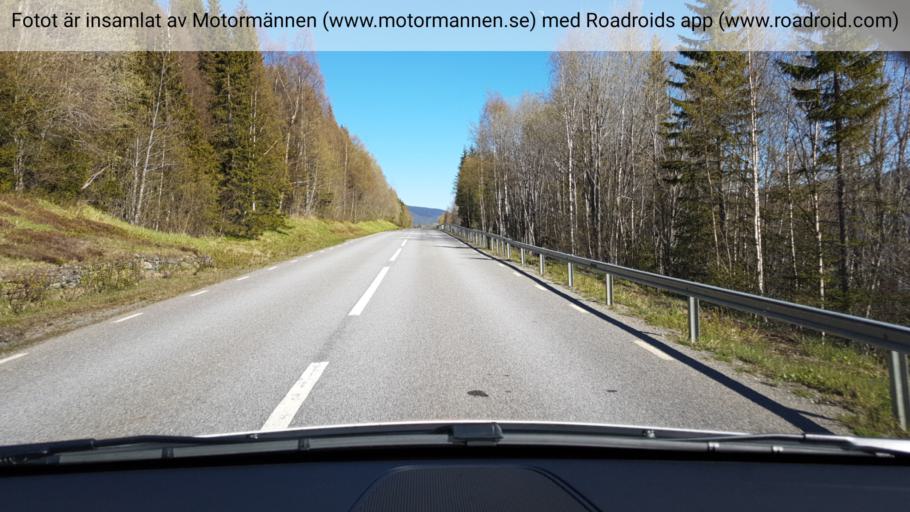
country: NO
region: Nord-Trondelag
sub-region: Lierne
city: Sandvika
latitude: 64.3843
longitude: 14.5407
